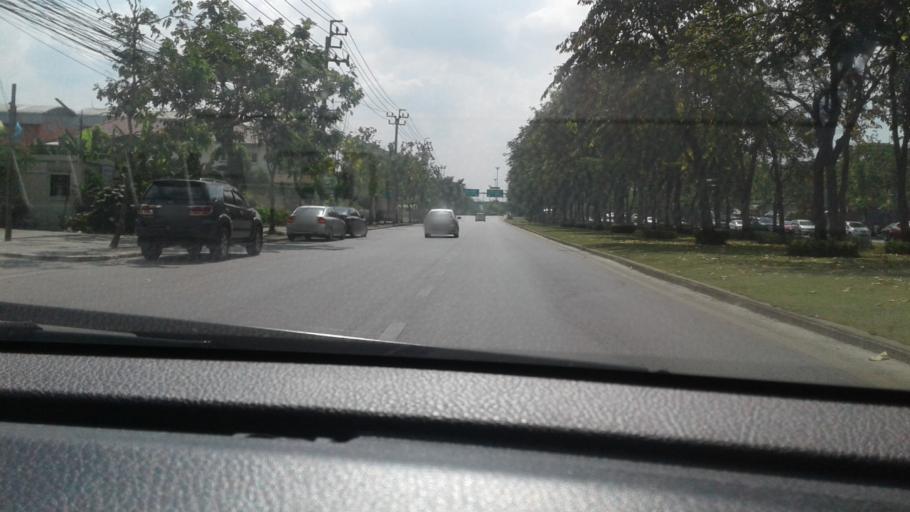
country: TH
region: Nonthaburi
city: Bang Yai
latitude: 13.7914
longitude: 100.3947
